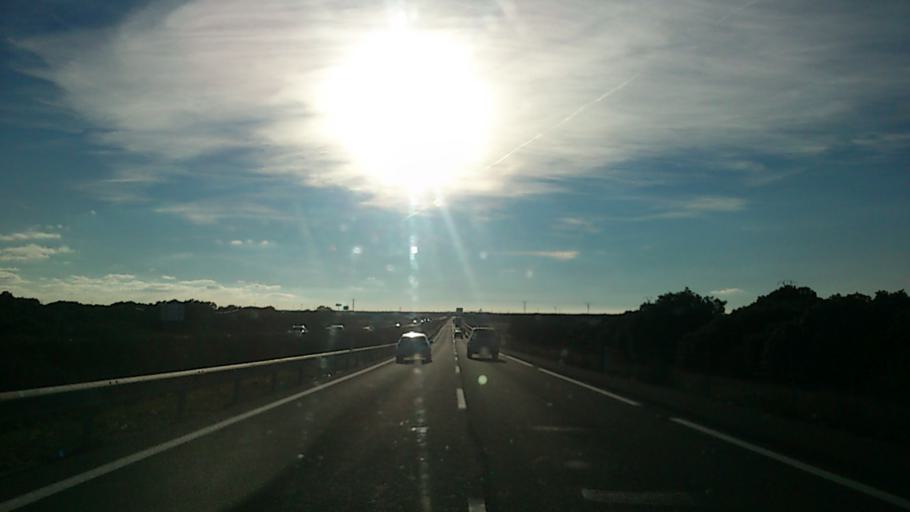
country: ES
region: Castille-La Mancha
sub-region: Provincia de Guadalajara
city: Mirabueno
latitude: 40.9369
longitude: -2.7048
